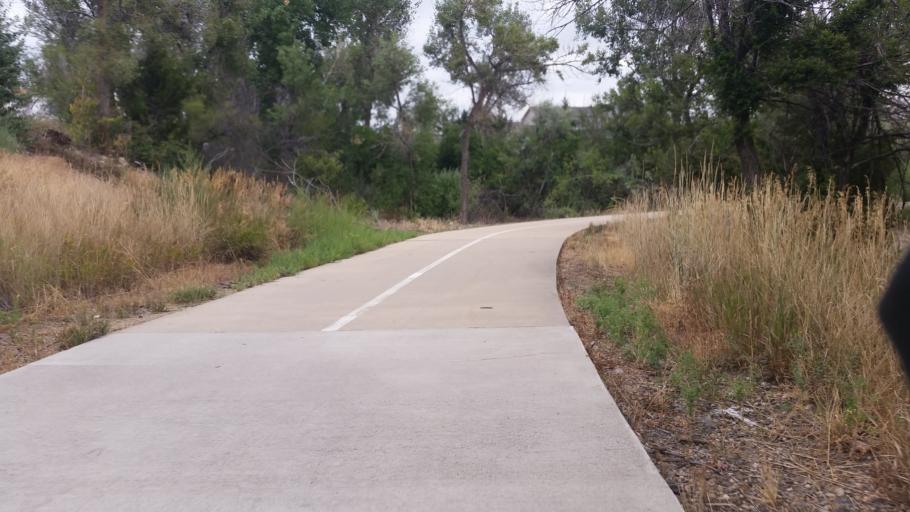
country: US
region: Colorado
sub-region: Adams County
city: Twin Lakes
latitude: 39.8158
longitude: -105.0037
